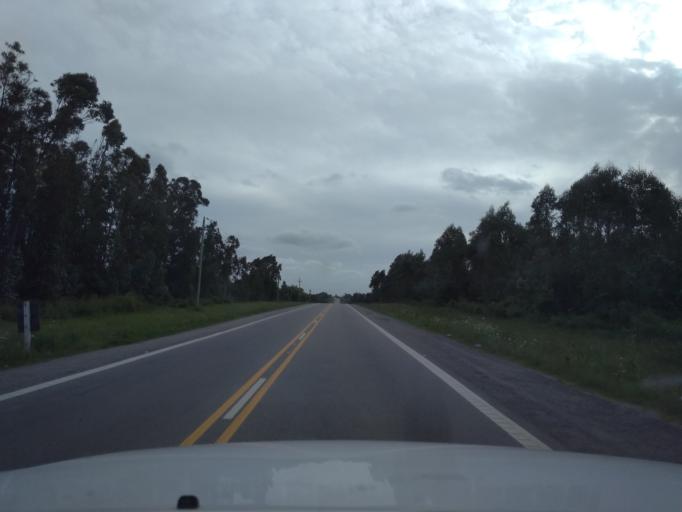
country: UY
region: Canelones
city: Joaquin Suarez
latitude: -34.6917
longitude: -56.0295
